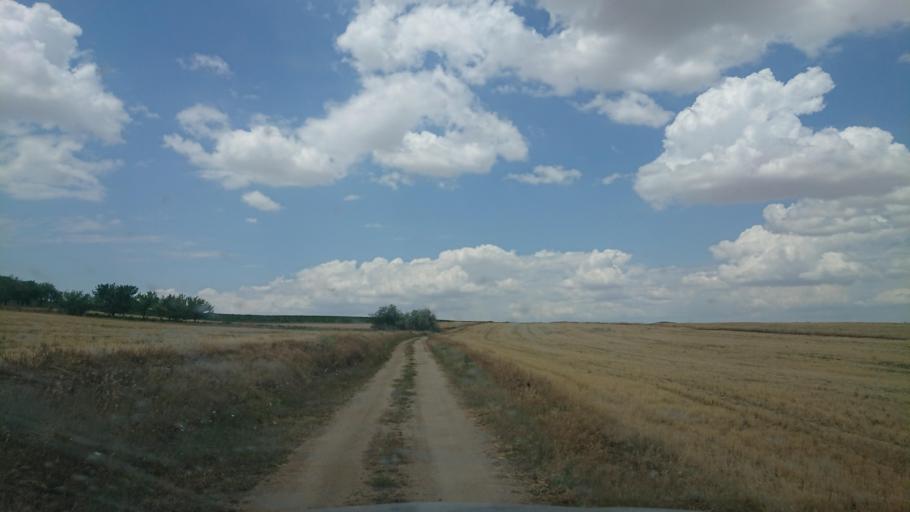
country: TR
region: Aksaray
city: Agacoren
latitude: 38.8941
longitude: 33.8830
